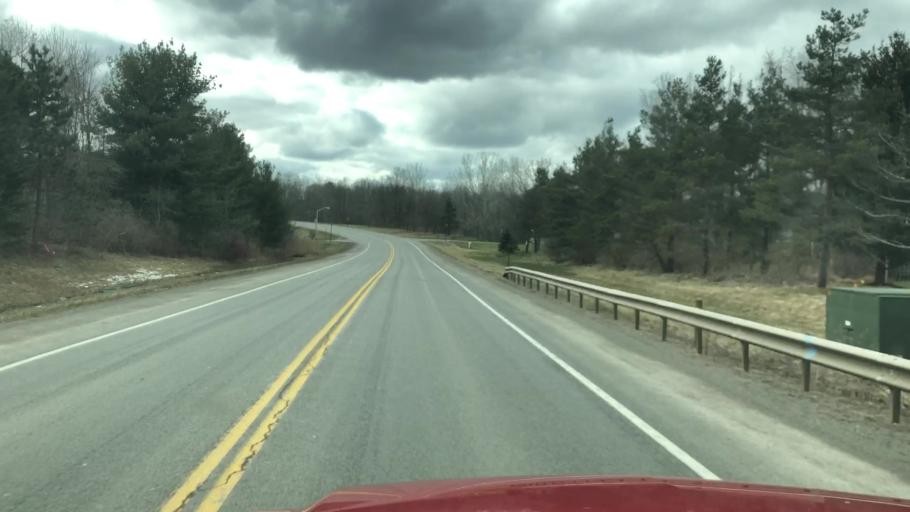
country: US
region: New York
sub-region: Wayne County
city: Macedon
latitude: 43.1271
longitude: -77.3484
